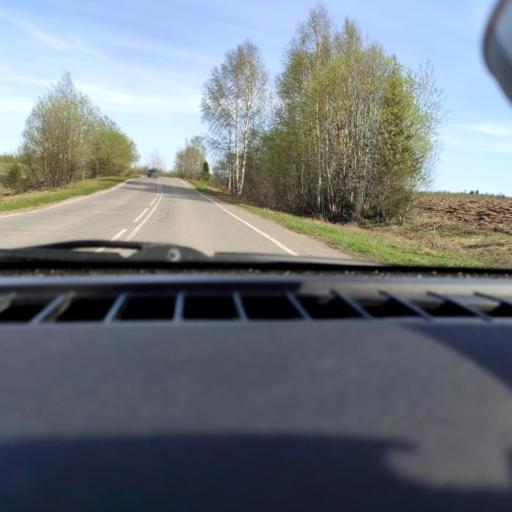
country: RU
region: Perm
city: Perm
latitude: 58.2487
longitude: 56.1340
